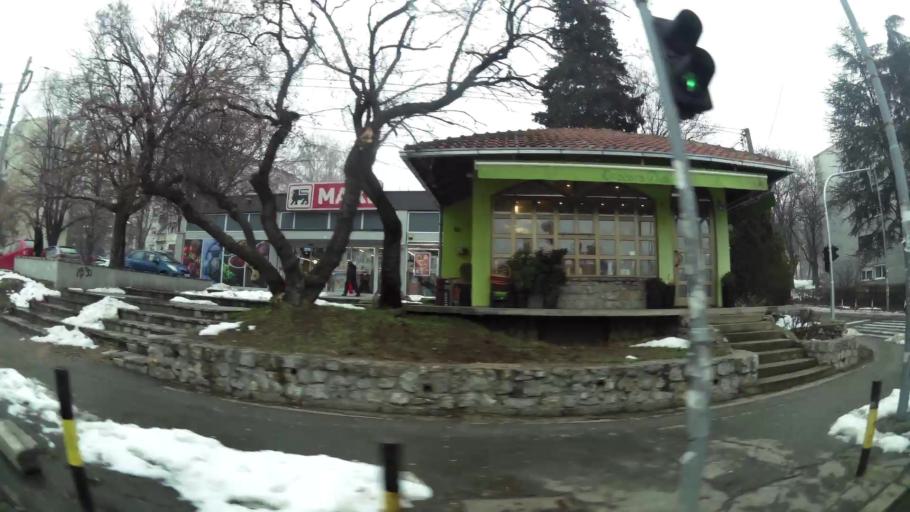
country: RS
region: Central Serbia
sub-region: Belgrade
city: Vozdovac
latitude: 44.7731
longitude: 20.4869
